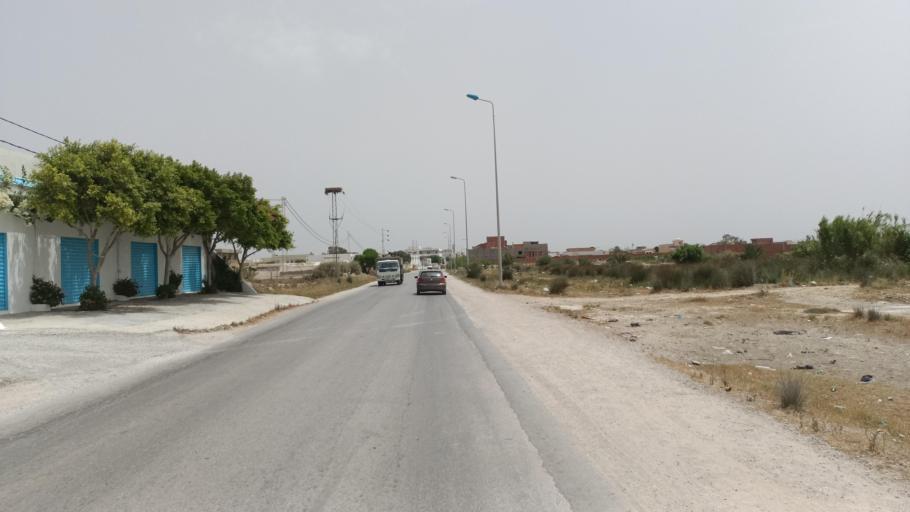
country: TN
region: Nabul
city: Manzil Bu Zalafah
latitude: 36.7101
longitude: 10.4828
